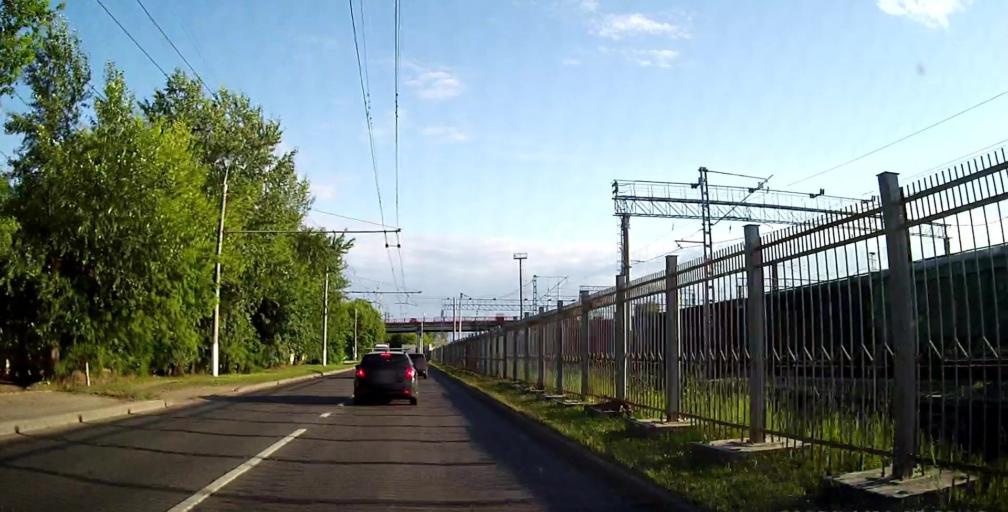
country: RU
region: Moskovskaya
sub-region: Podol'skiy Rayon
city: Podol'sk
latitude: 55.4267
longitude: 37.5633
